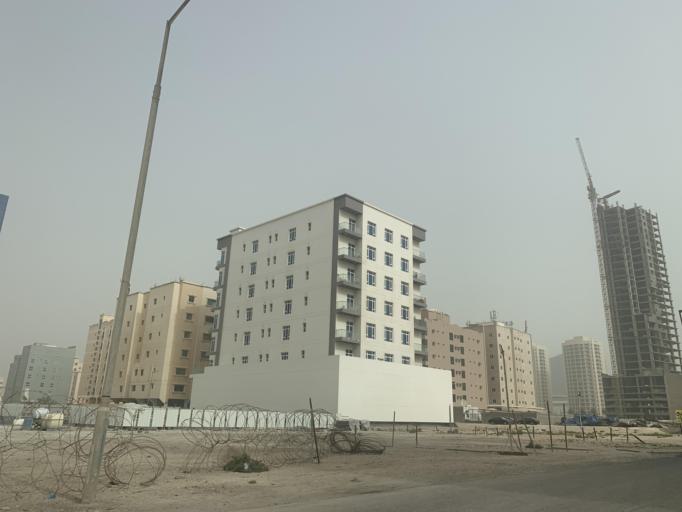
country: BH
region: Manama
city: Jidd Hafs
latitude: 26.2262
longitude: 50.5585
